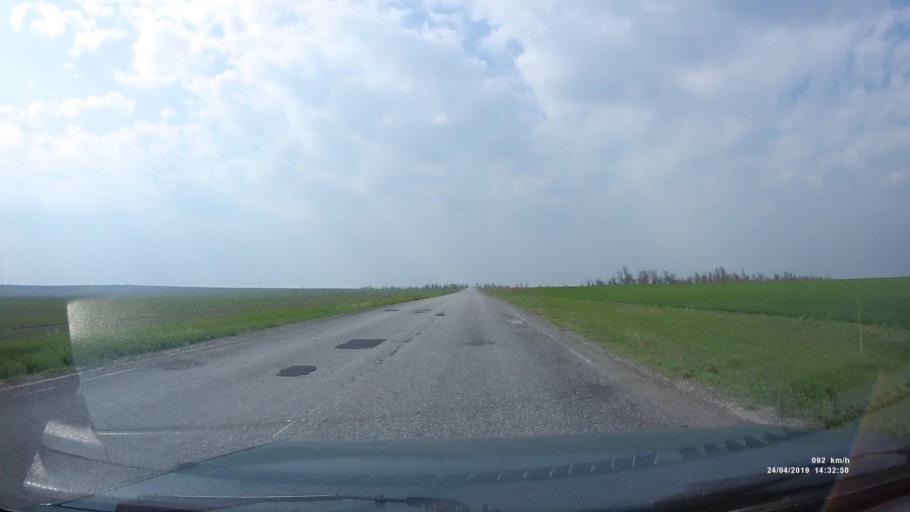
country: RU
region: Kalmykiya
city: Arshan'
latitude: 46.3682
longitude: 43.9628
